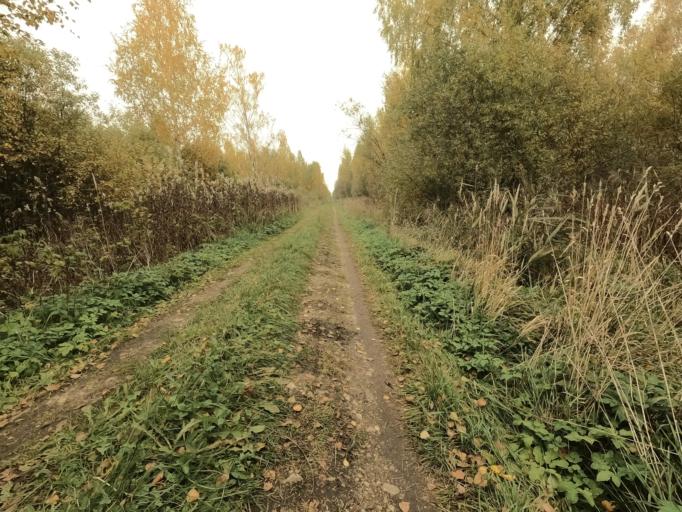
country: RU
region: Novgorod
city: Pankovka
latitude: 58.8824
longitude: 30.9443
